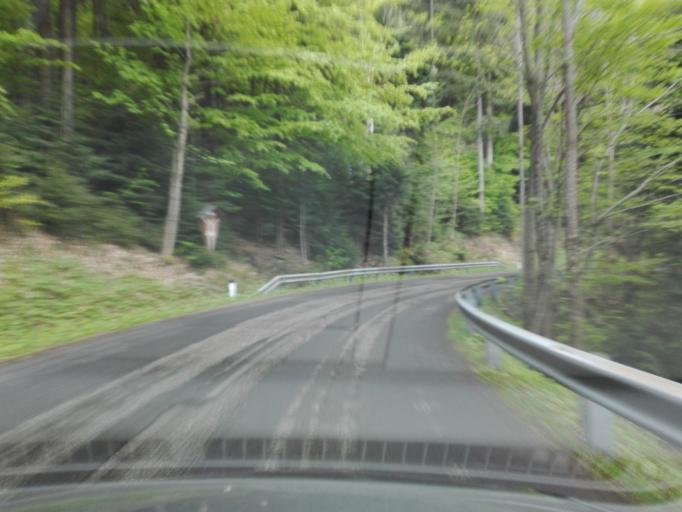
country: DE
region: Bavaria
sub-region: Lower Bavaria
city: Obernzell
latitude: 48.5207
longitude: 13.6715
